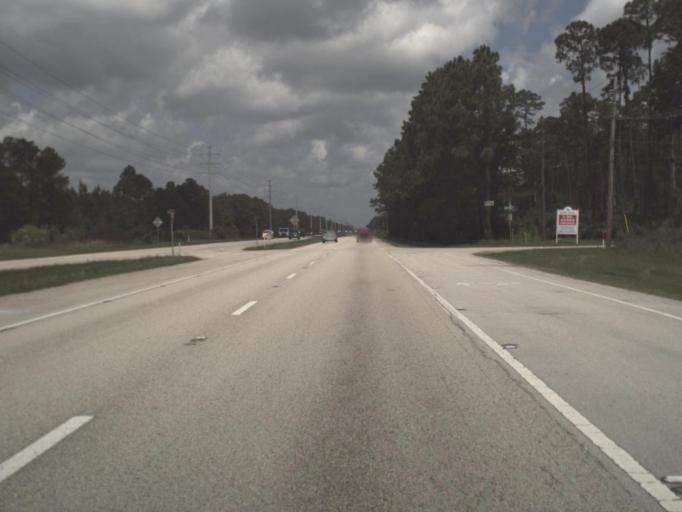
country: US
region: Florida
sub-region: Saint Johns County
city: Villano Beach
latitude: 30.0158
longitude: -81.3949
